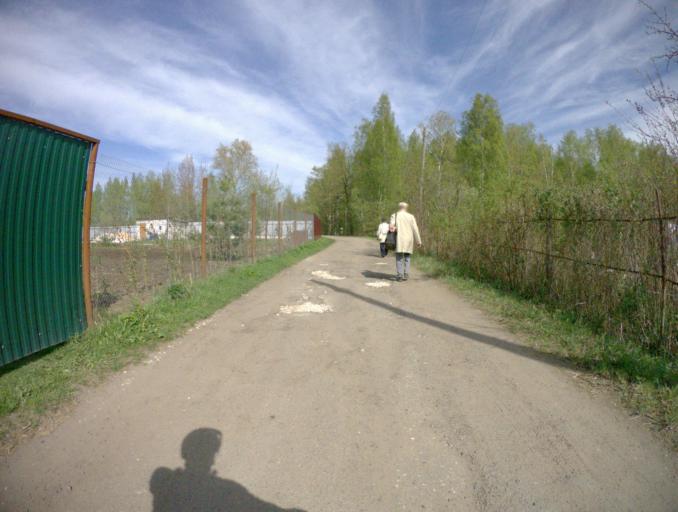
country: RU
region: Vladimir
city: Orgtrud
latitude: 56.1980
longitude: 40.5890
